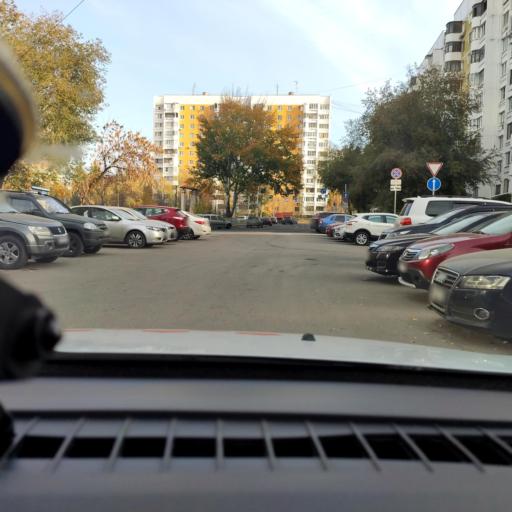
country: RU
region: Samara
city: Samara
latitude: 53.1882
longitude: 50.1360
